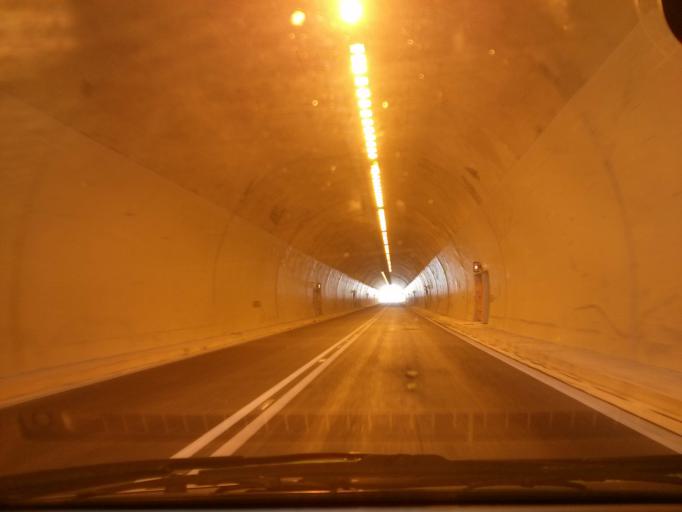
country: GR
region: Crete
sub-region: Nomos Lasithiou
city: Agios Nikolaos
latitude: 35.1608
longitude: 25.7078
